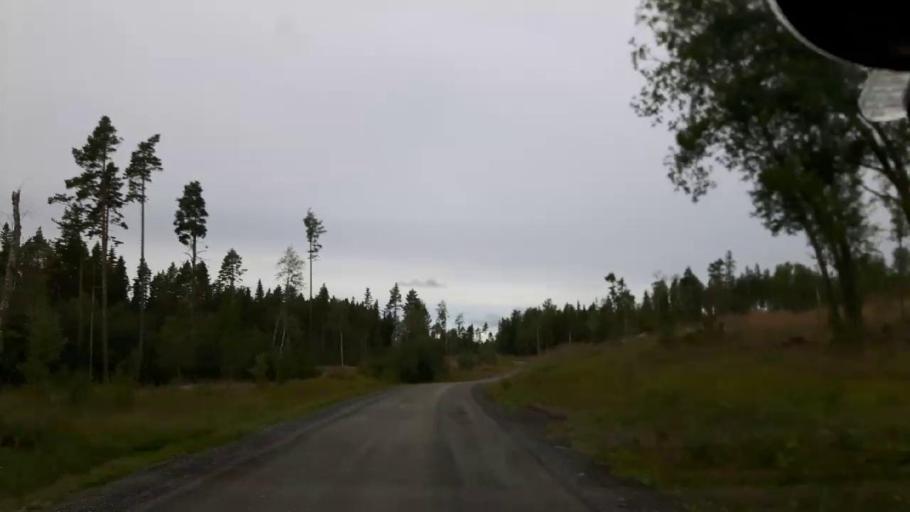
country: SE
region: Jaemtland
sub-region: Krokoms Kommun
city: Krokom
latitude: 63.2791
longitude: 14.3917
